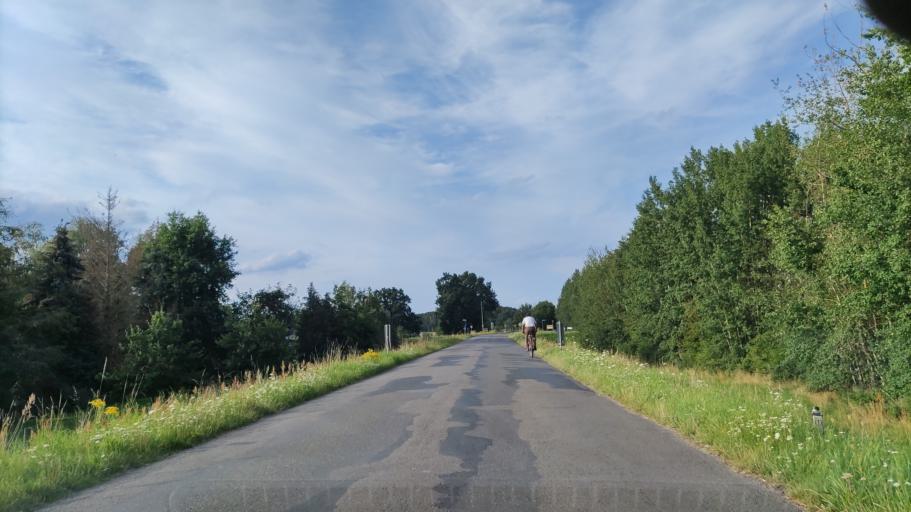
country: DE
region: Lower Saxony
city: Dannenberg
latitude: 53.1054
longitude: 11.1093
